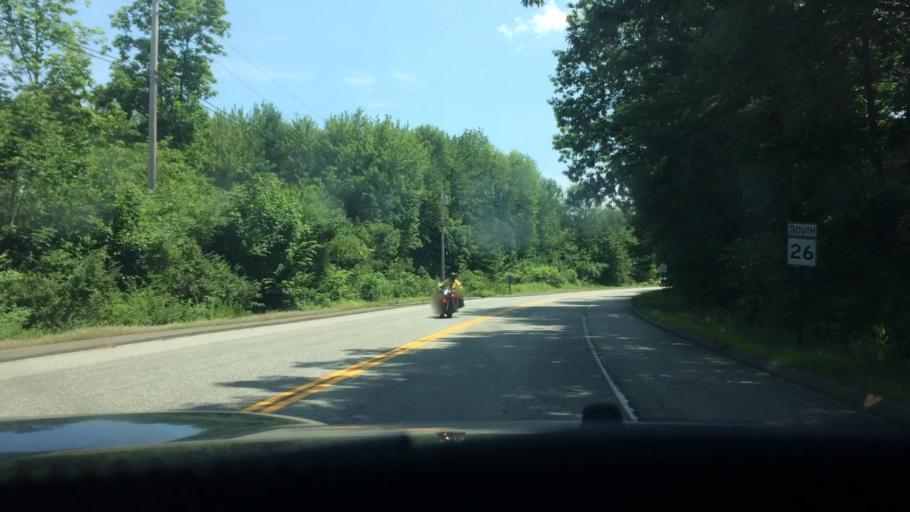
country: US
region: Maine
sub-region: Androscoggin County
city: Poland
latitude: 44.0362
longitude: -70.3702
